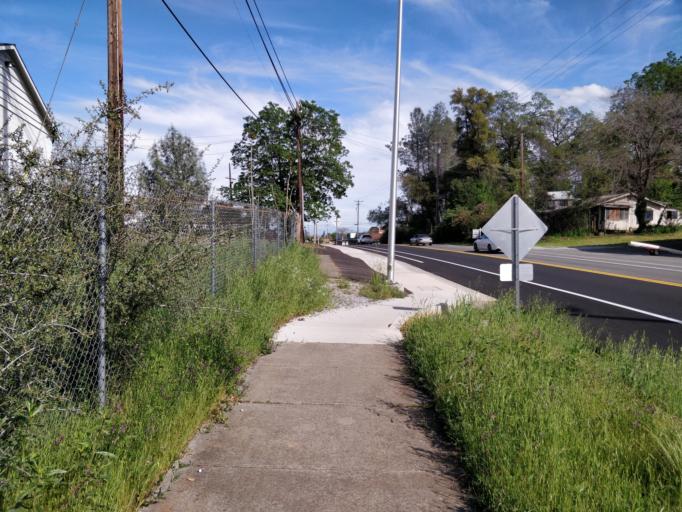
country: US
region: California
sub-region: Shasta County
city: Central Valley (historical)
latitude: 40.6817
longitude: -122.3748
